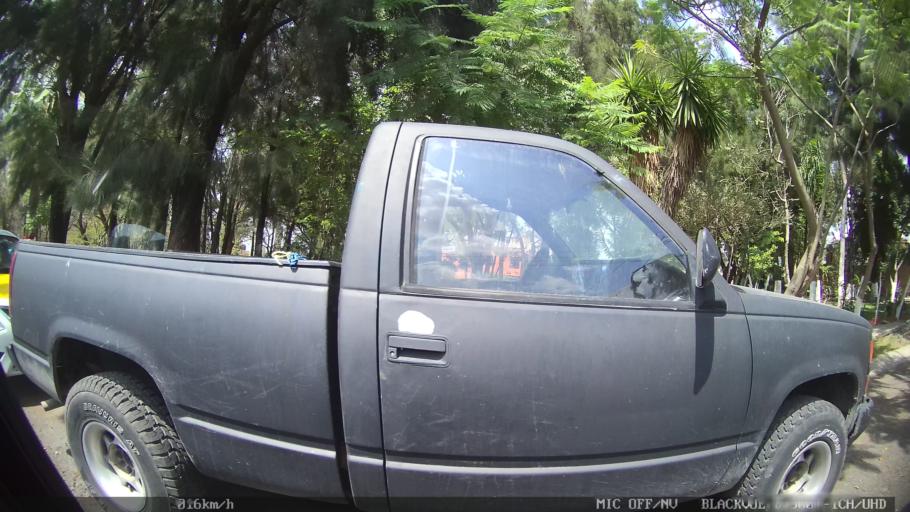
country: MX
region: Jalisco
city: Tonala
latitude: 20.6230
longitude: -103.2600
